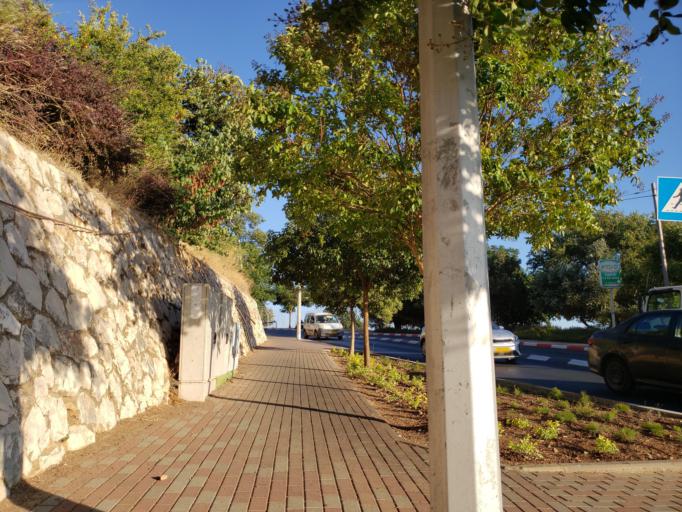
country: IL
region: Northern District
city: Safed
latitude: 32.9577
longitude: 35.4915
